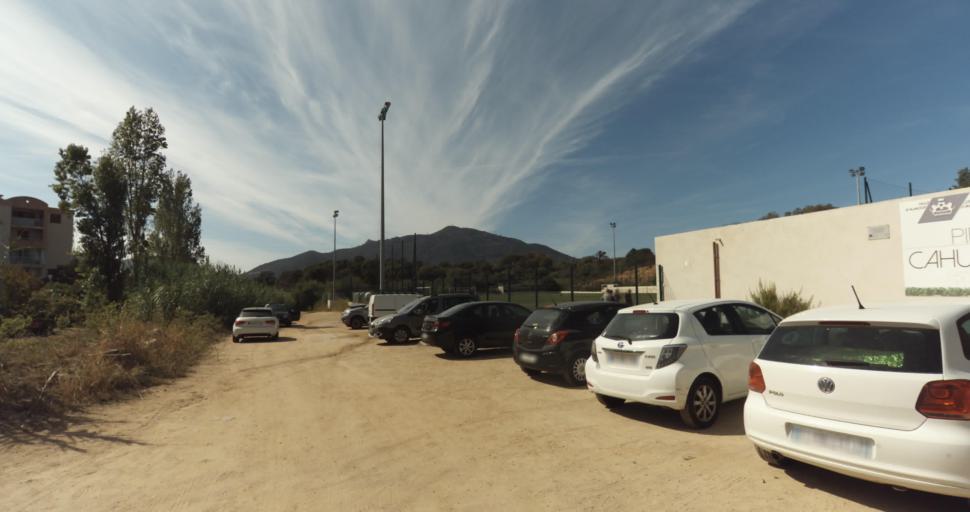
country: FR
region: Corsica
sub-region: Departement de la Corse-du-Sud
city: Ajaccio
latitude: 41.9416
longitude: 8.7642
